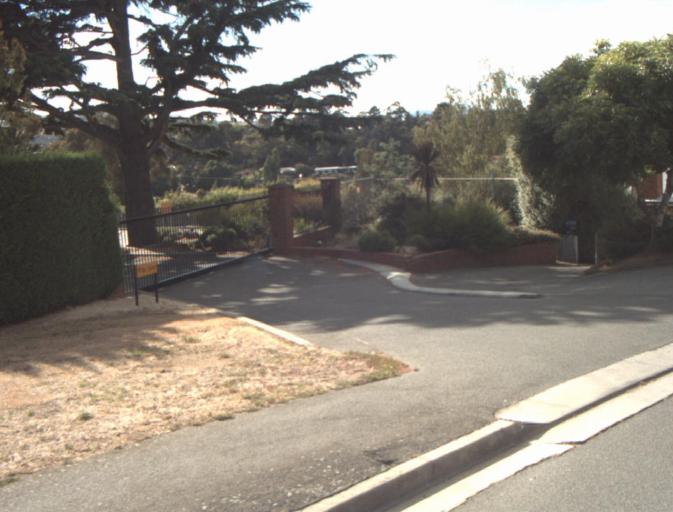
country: AU
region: Tasmania
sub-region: Launceston
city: Newstead
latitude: -41.4495
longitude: 147.1686
